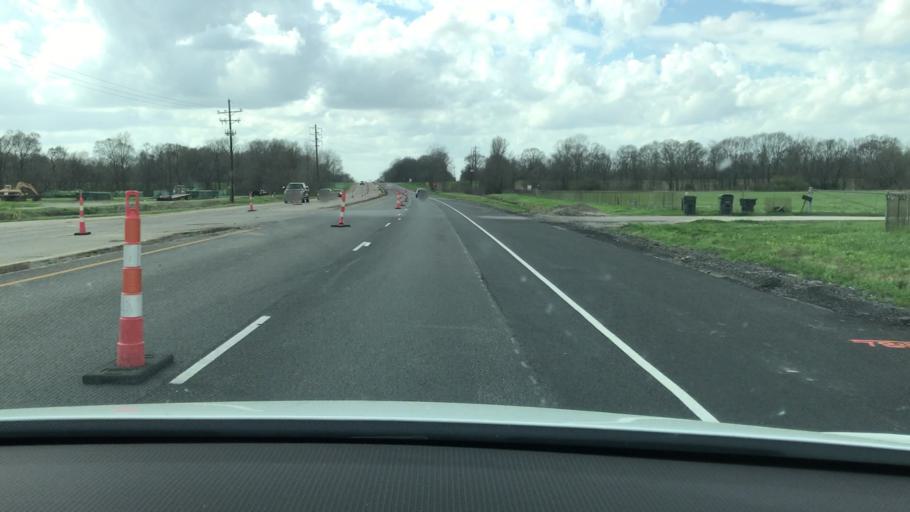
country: US
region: Louisiana
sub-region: Pointe Coupee Parish
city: Livonia
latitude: 30.5571
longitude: -91.6530
